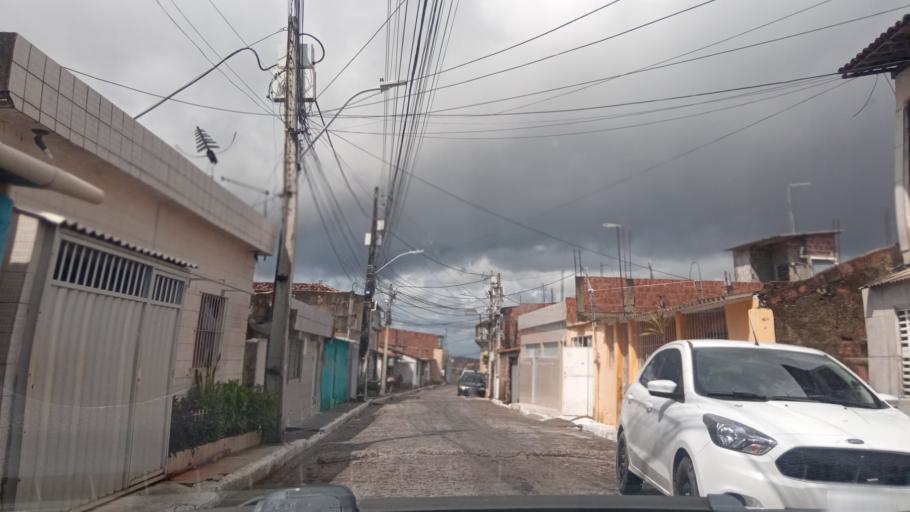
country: BR
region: Pernambuco
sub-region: Jaboatao Dos Guararapes
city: Jaboatao dos Guararapes
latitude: -8.1318
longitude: -34.9537
